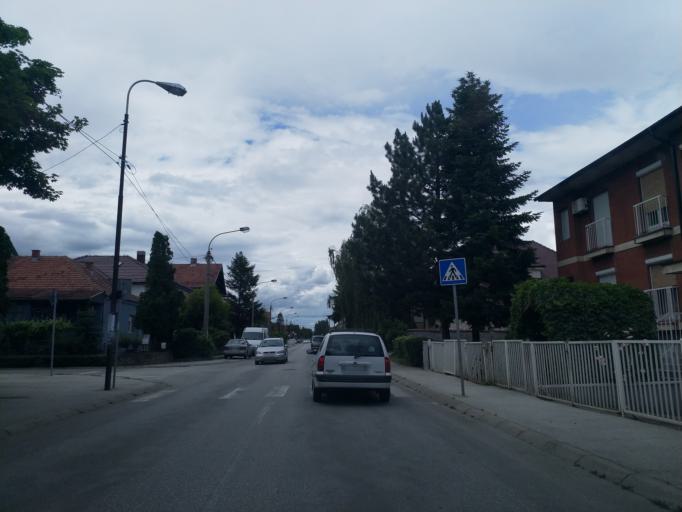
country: RS
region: Central Serbia
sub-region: Pomoravski Okrug
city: Jagodina
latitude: 43.9704
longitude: 21.2748
